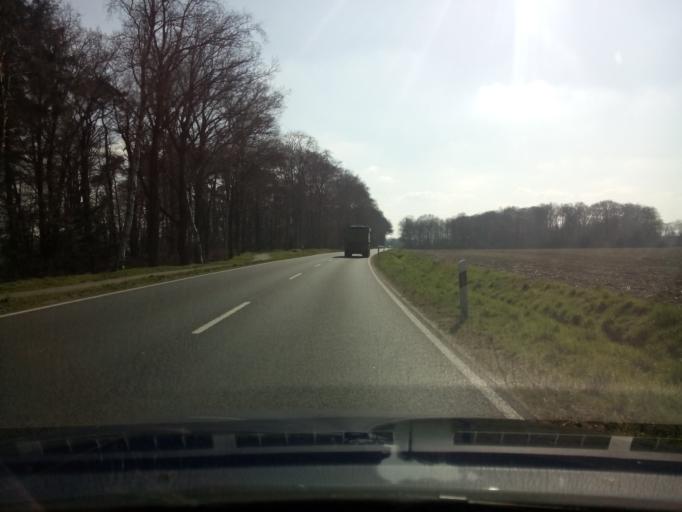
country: DE
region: Lower Saxony
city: Isterberg
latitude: 52.3355
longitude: 7.0704
